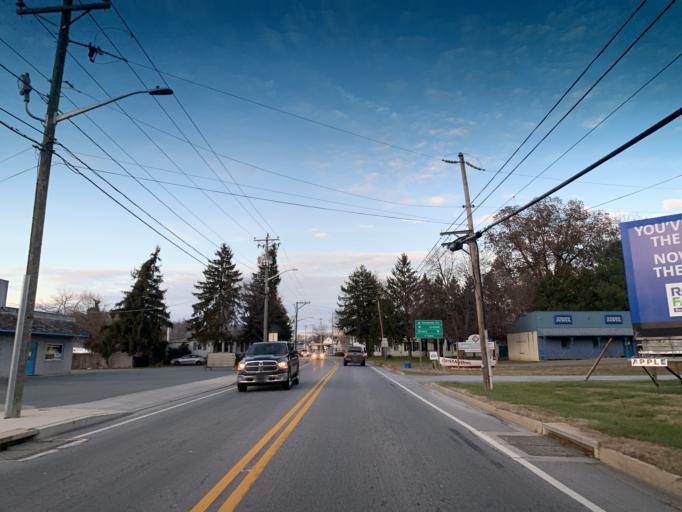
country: US
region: Delaware
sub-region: New Castle County
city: Middletown
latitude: 39.4021
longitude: -75.8683
